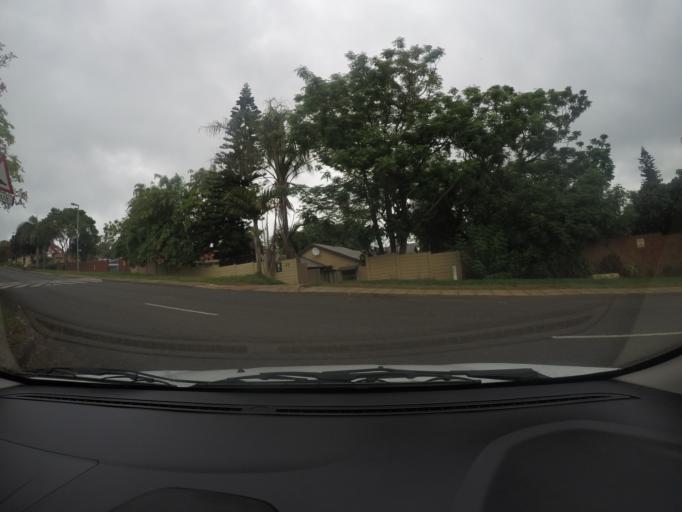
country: ZA
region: KwaZulu-Natal
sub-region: uThungulu District Municipality
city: Empangeni
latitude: -28.7614
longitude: 31.8920
